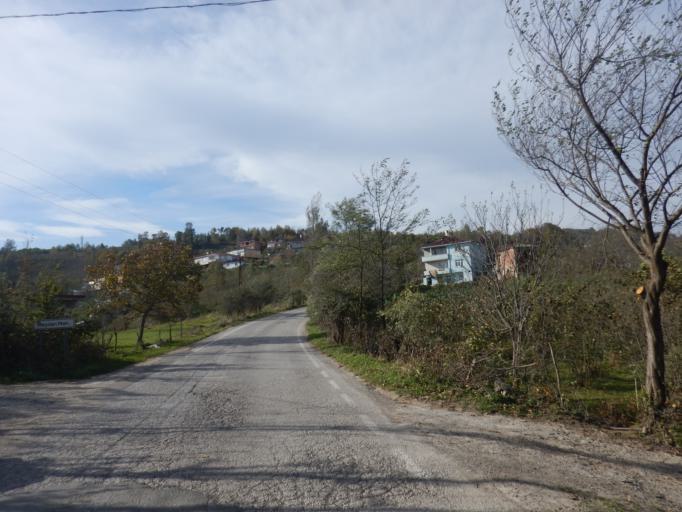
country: TR
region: Ordu
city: Golkoy
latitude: 40.6903
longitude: 37.5953
